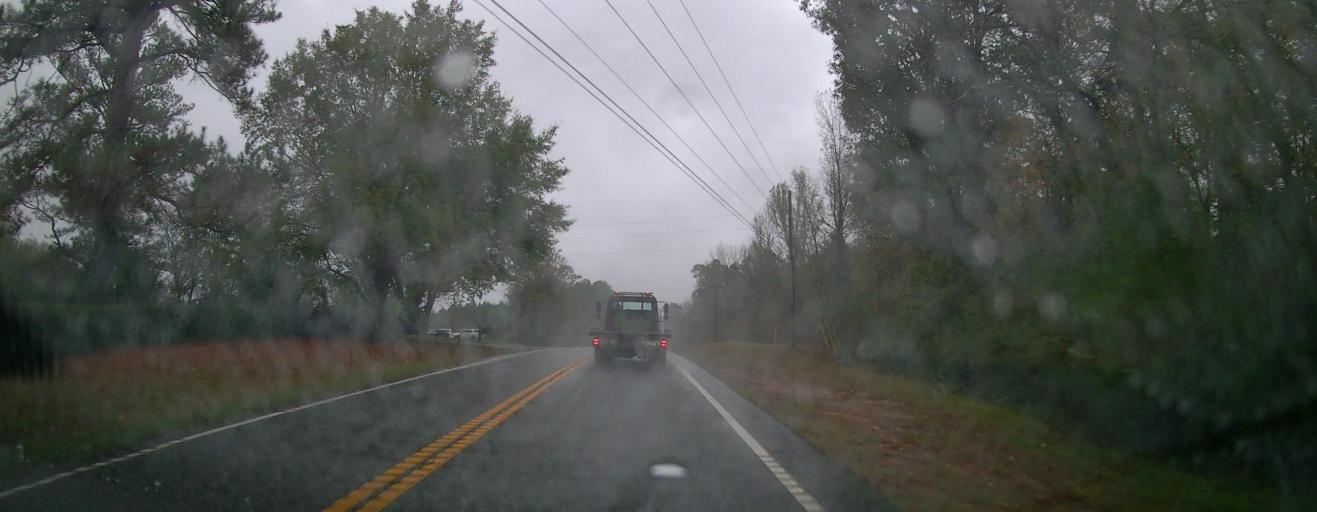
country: US
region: Georgia
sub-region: Jones County
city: Gray
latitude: 33.0586
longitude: -83.4982
